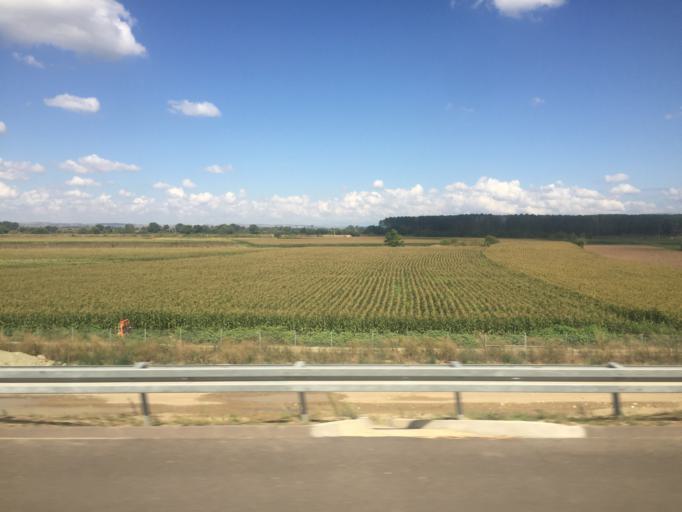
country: TR
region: Bursa
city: Karacabey
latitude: 40.1388
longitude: 28.2998
